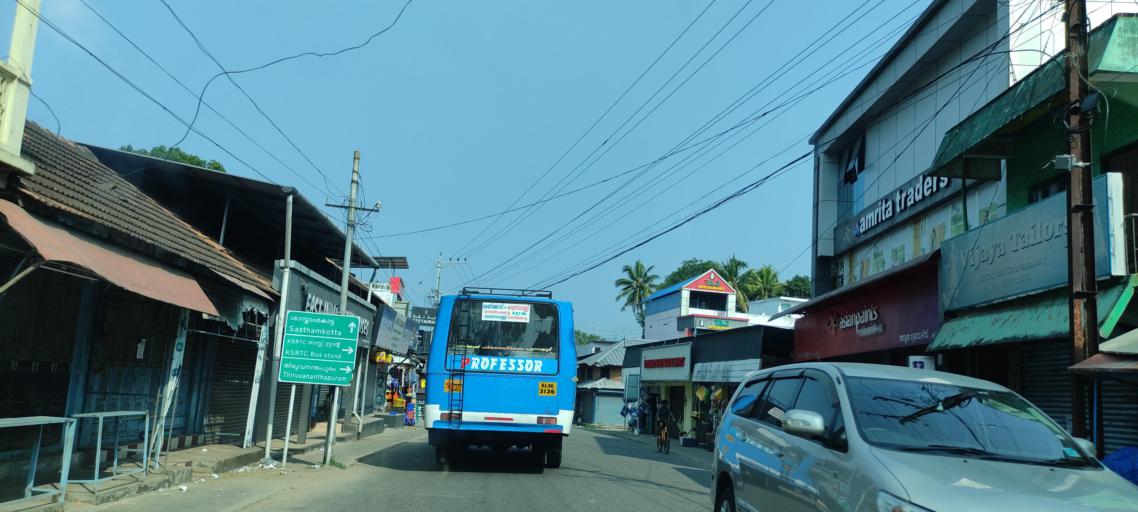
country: IN
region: Kerala
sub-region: Kollam
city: Panmana
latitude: 9.0565
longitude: 76.5399
